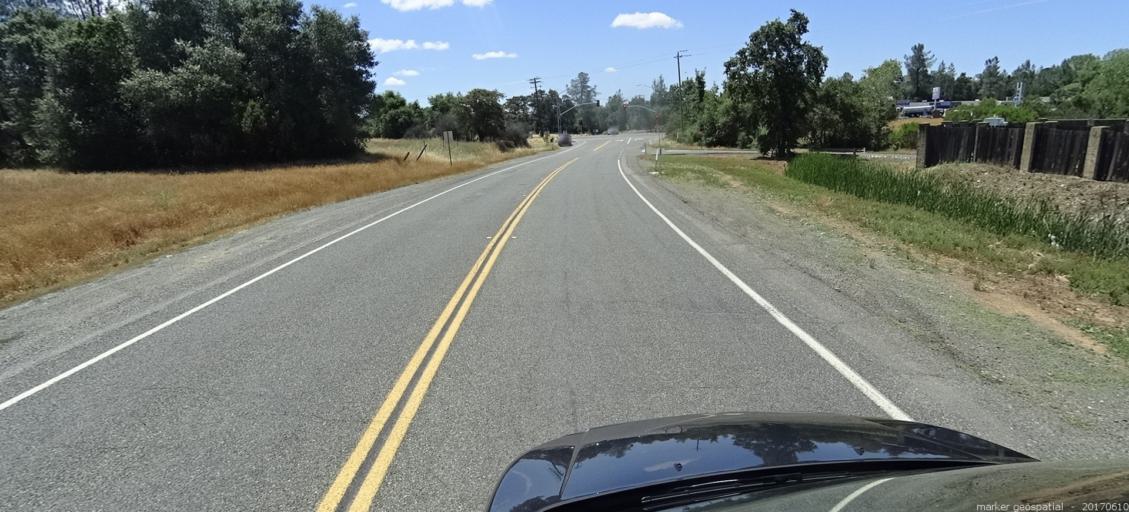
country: US
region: California
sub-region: Butte County
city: Oroville East
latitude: 39.5049
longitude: -121.4600
